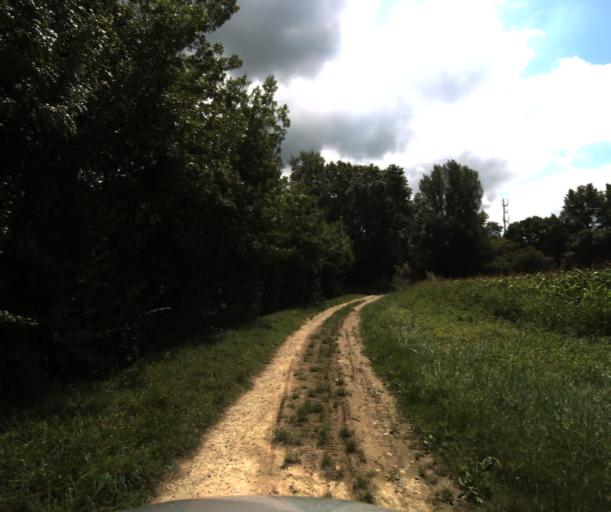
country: FR
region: Midi-Pyrenees
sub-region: Departement de la Haute-Garonne
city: Lacasse
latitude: 43.4054
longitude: 1.2703
